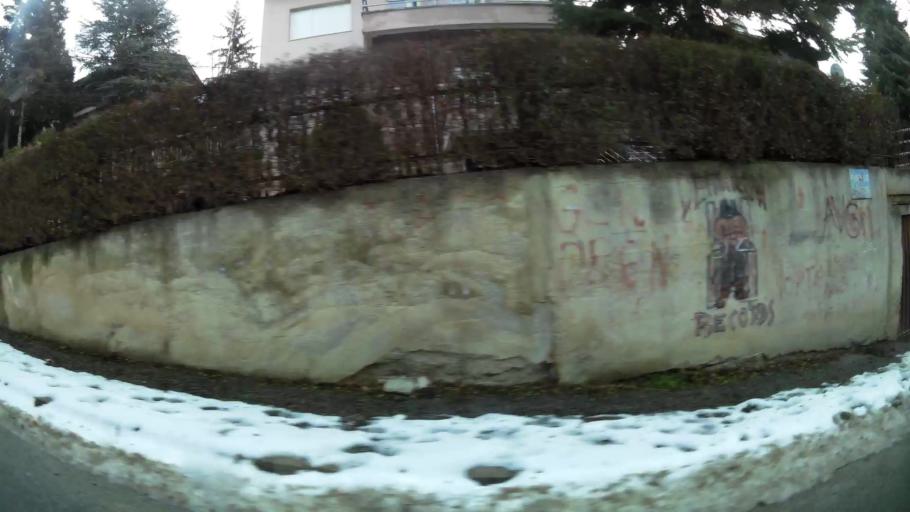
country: XK
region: Pristina
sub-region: Komuna e Prishtines
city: Pristina
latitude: 42.6684
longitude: 21.1787
